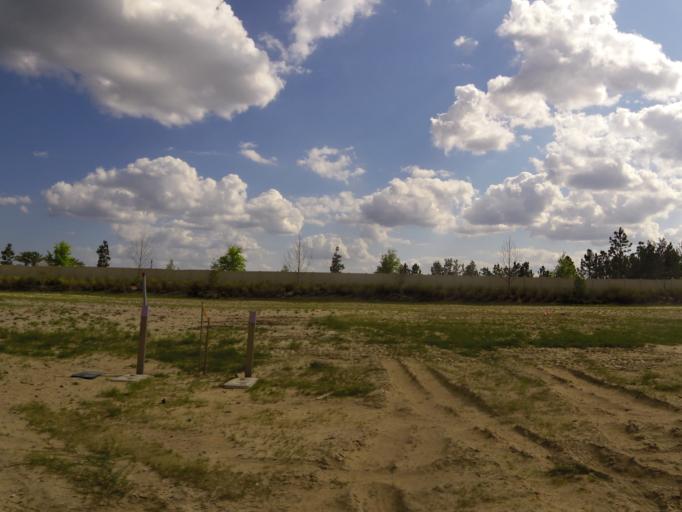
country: US
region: Florida
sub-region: Saint Johns County
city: Palm Valley
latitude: 30.1711
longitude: -81.5077
